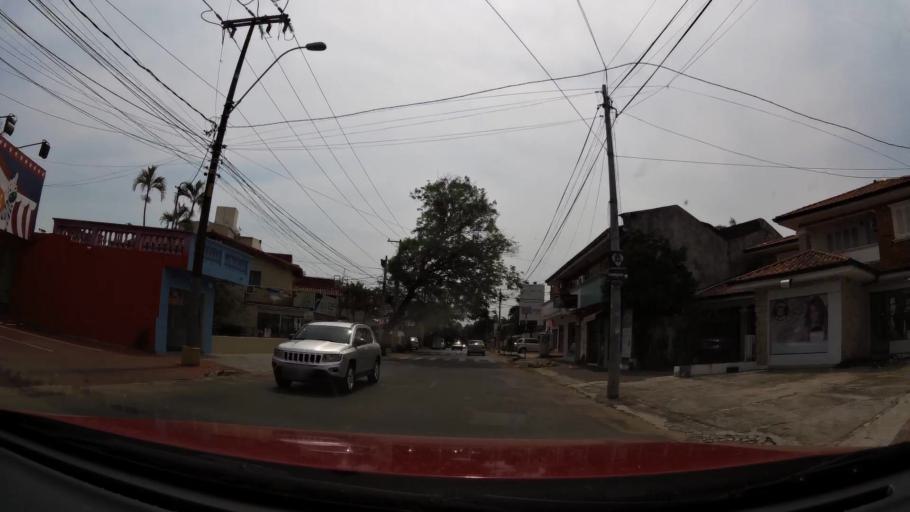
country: PY
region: Asuncion
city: Asuncion
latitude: -25.2891
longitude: -57.5749
